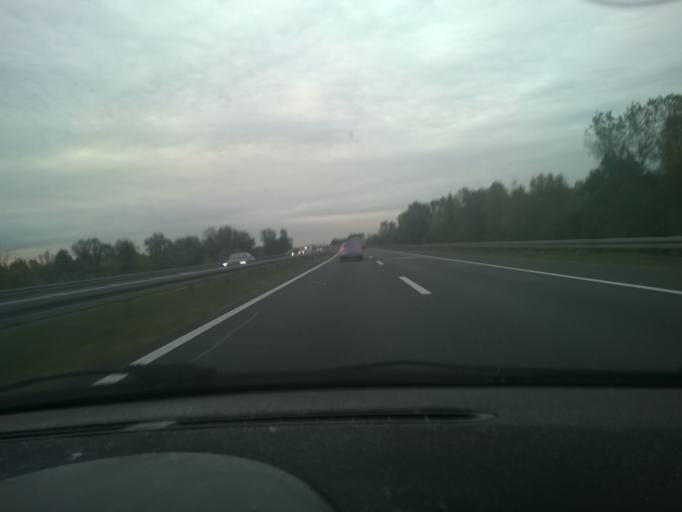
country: HR
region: Zagrebacka
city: Bestovje
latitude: 45.8167
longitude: 15.8243
